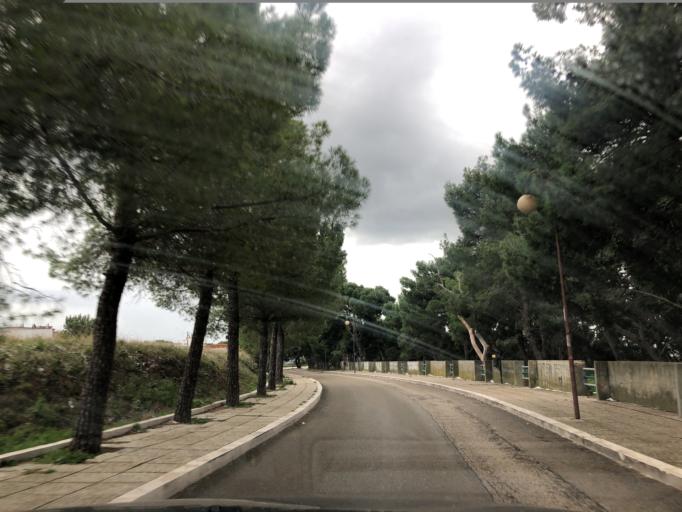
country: IT
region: Apulia
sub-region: Provincia di Foggia
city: Lucera
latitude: 41.5072
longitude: 15.3238
